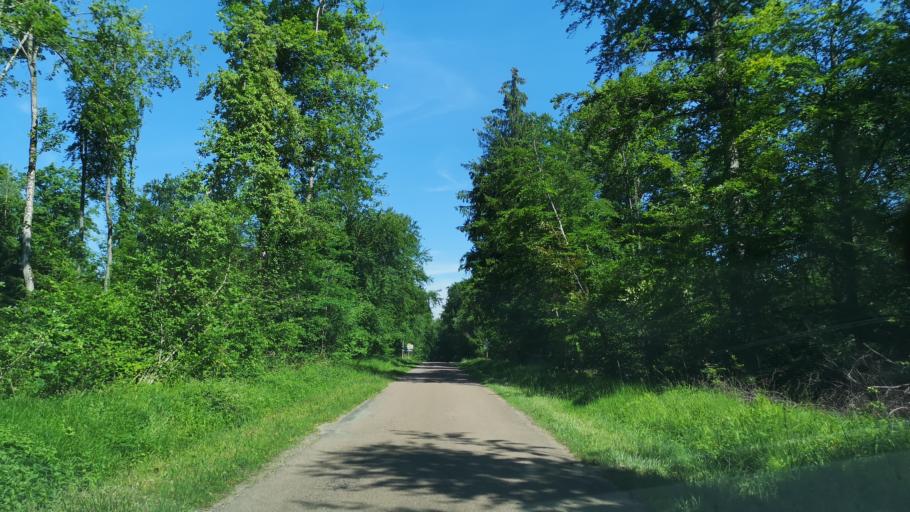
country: FR
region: Lorraine
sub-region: Departement de la Meuse
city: Vigneulles-les-Hattonchatel
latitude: 49.0299
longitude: 5.6415
